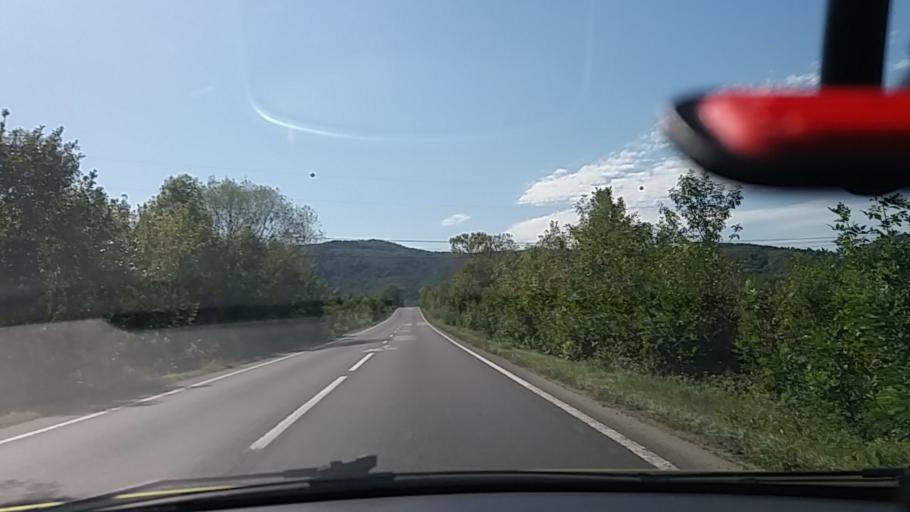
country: RO
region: Hunedoara
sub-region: Comuna Zam
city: Zam
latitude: 45.9873
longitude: 22.4341
